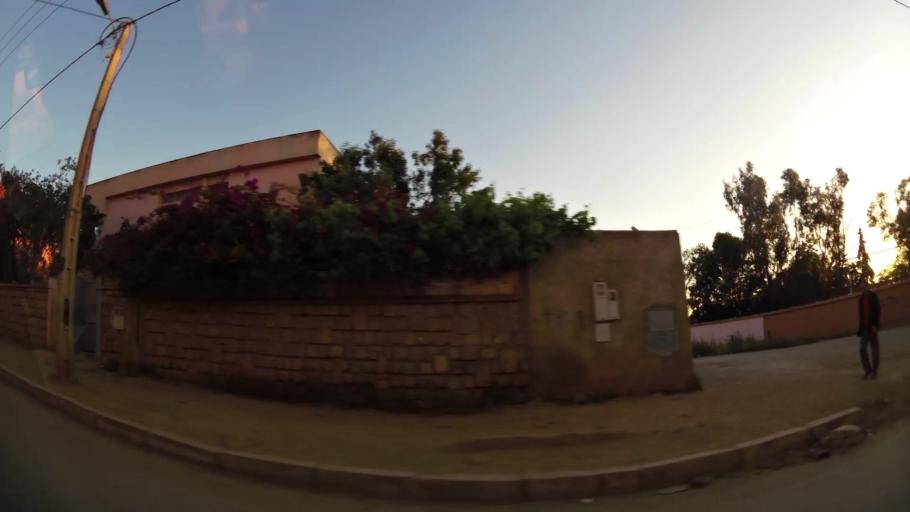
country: MA
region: Oriental
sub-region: Berkane-Taourirt
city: Berkane
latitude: 34.9177
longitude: -2.3248
